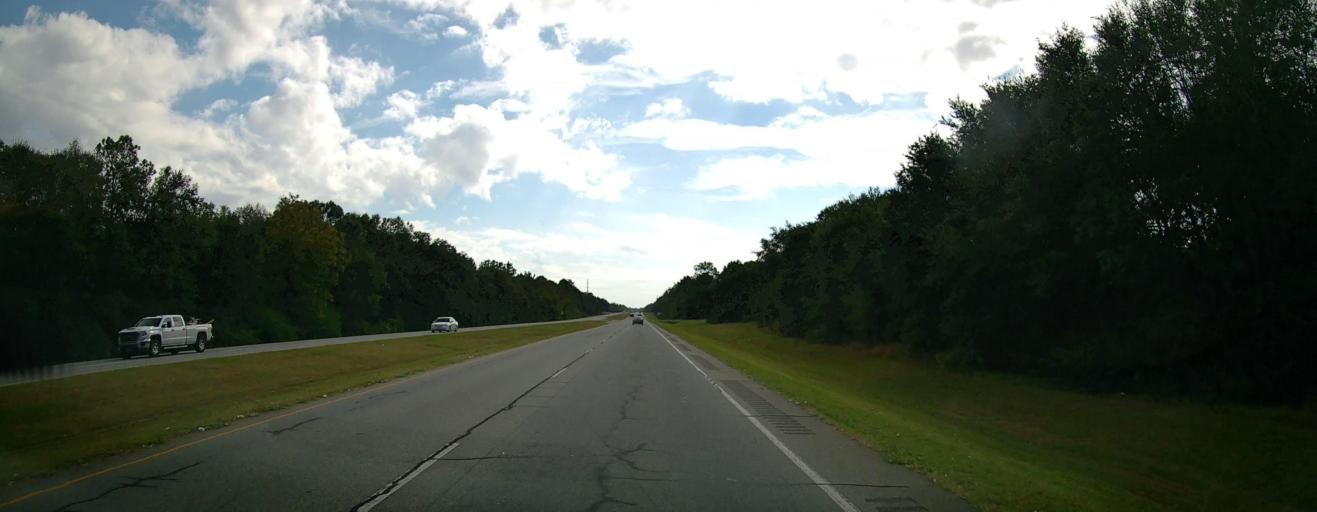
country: US
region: Georgia
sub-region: Mitchell County
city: Camilla
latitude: 31.2690
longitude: -84.1931
